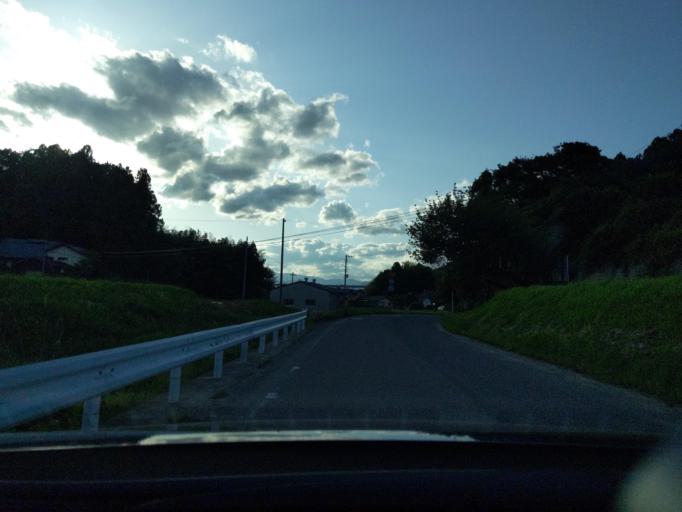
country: JP
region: Fukushima
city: Miharu
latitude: 37.4317
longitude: 140.4342
